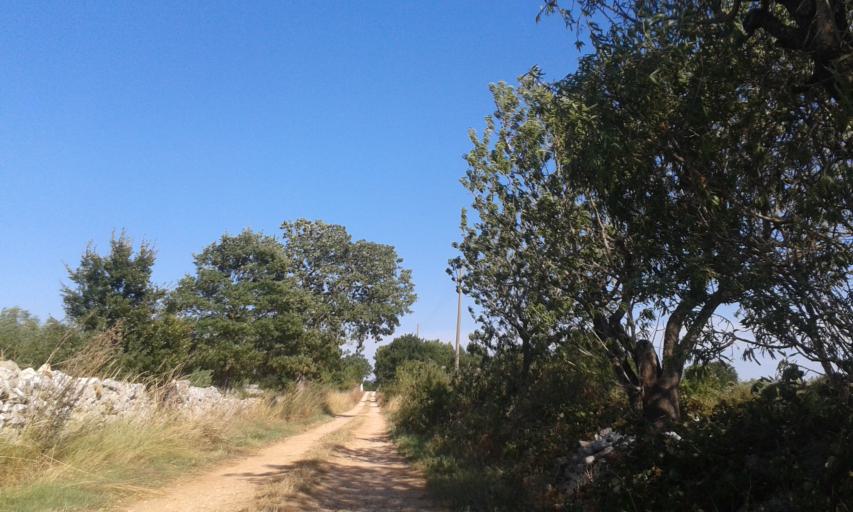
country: IT
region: Apulia
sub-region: Provincia di Bari
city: Gioia del Colle
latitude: 40.7750
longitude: 16.9683
